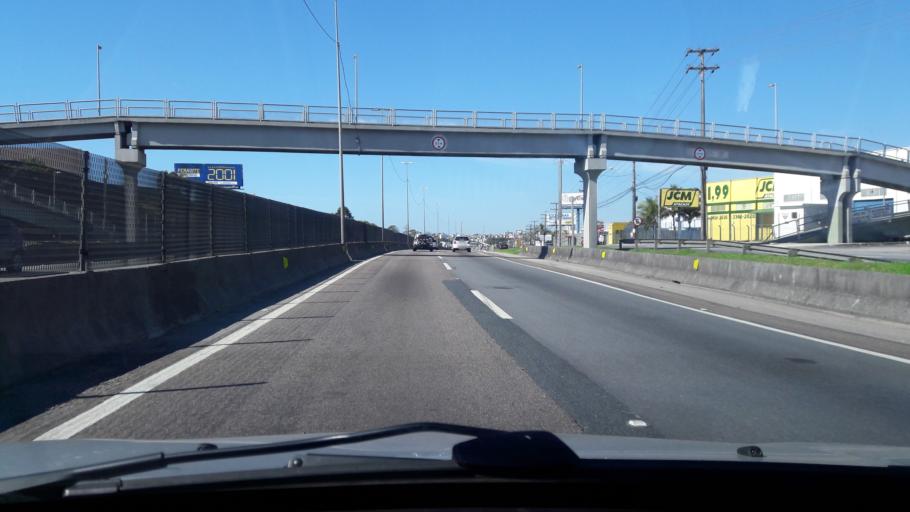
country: BR
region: Santa Catarina
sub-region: Sao Jose
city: Campinas
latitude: -27.5454
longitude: -48.6201
